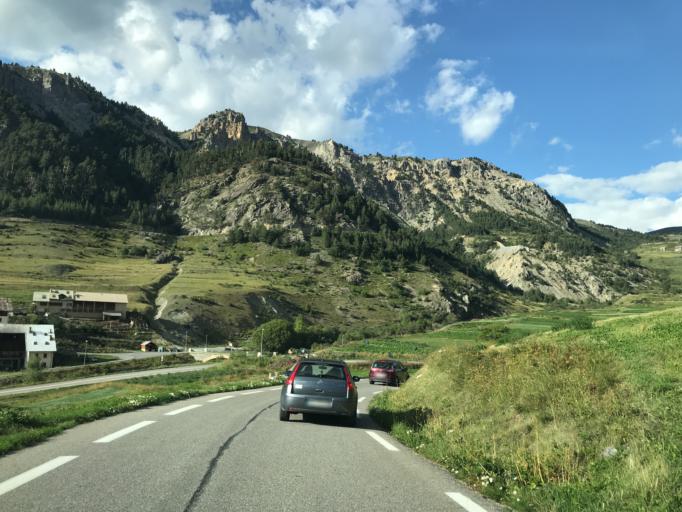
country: IT
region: Piedmont
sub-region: Provincia di Torino
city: Claviere
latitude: 44.8688
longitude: 6.7255
